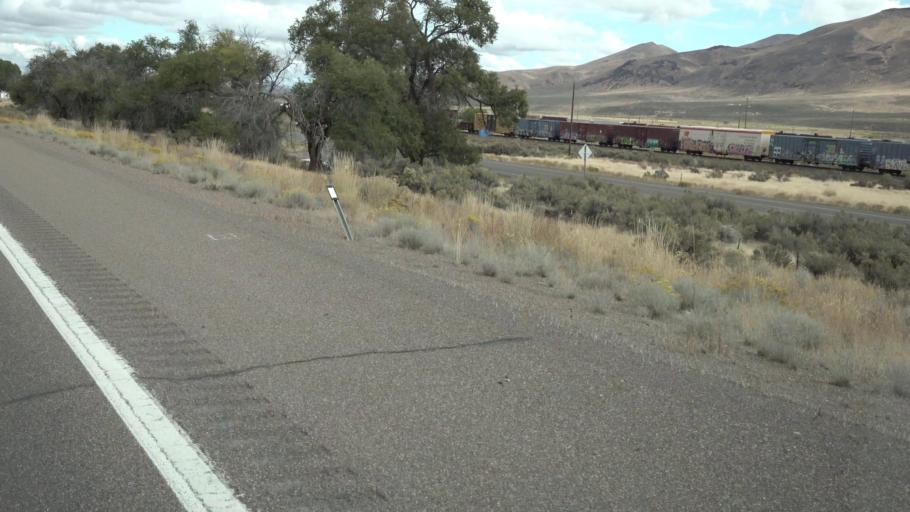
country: US
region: Nevada
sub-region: Elko County
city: Elko
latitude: 40.8819
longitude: -115.7157
